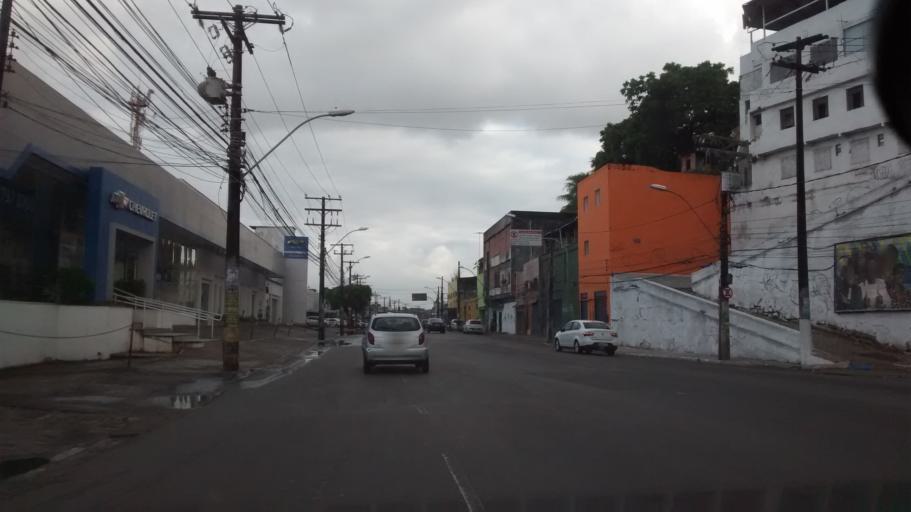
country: BR
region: Bahia
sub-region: Salvador
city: Salvador
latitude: -12.9571
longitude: -38.5020
